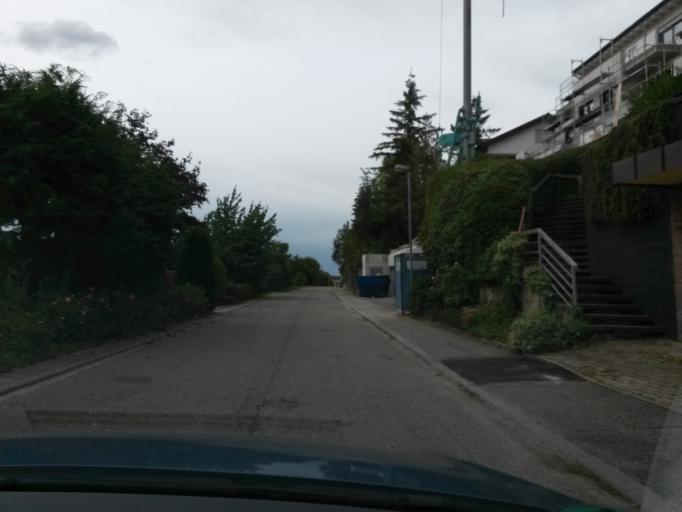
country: DE
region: Baden-Wuerttemberg
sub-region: Karlsruhe Region
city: Konigsbach-Stein
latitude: 48.9615
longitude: 8.6246
